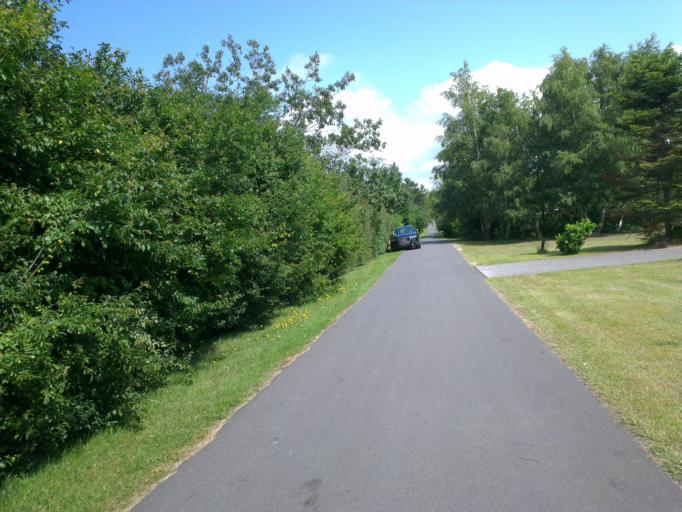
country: DK
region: Capital Region
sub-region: Halsnaes Kommune
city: Hundested
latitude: 55.9186
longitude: 11.9093
